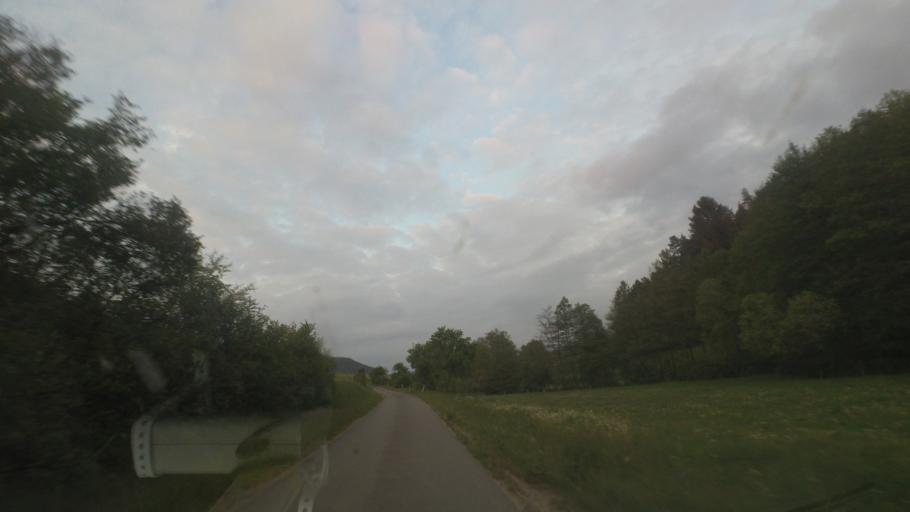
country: DE
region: Thuringia
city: Rottenbach
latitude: 50.7142
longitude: 11.1427
